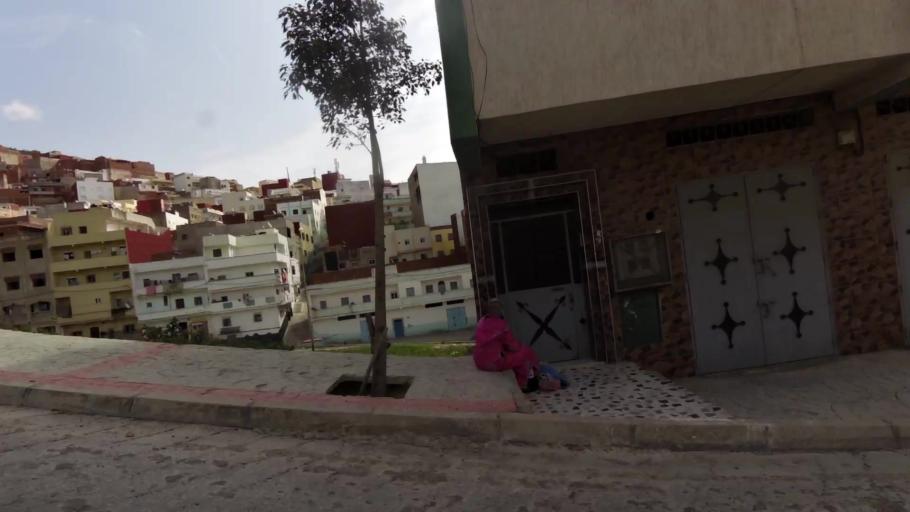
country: MA
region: Tanger-Tetouan
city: Tetouan
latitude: 35.5786
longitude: -5.3910
